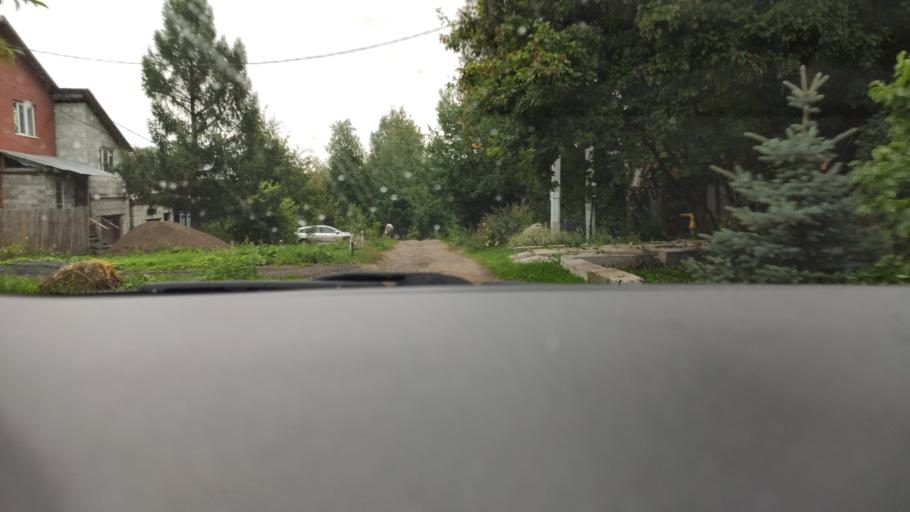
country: RU
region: Perm
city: Perm
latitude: 58.0198
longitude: 56.3192
